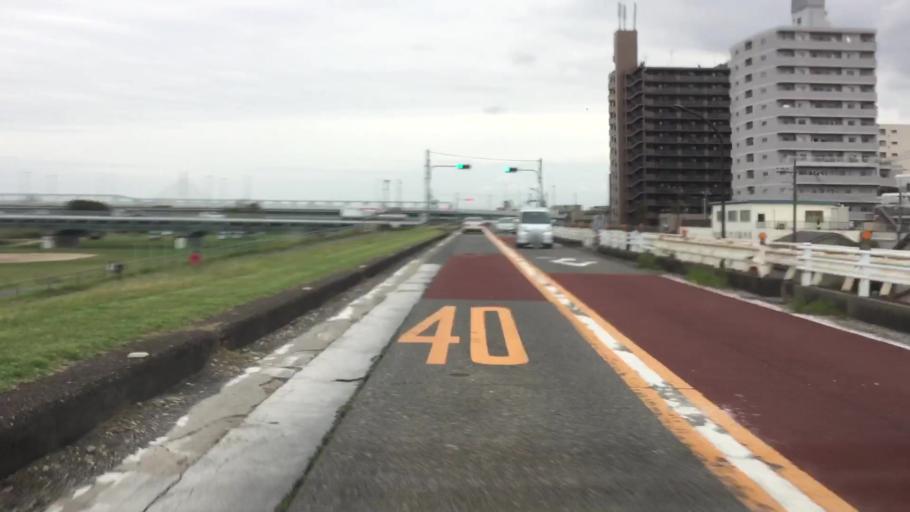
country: JP
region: Tokyo
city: Urayasu
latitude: 35.7318
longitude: 139.8259
